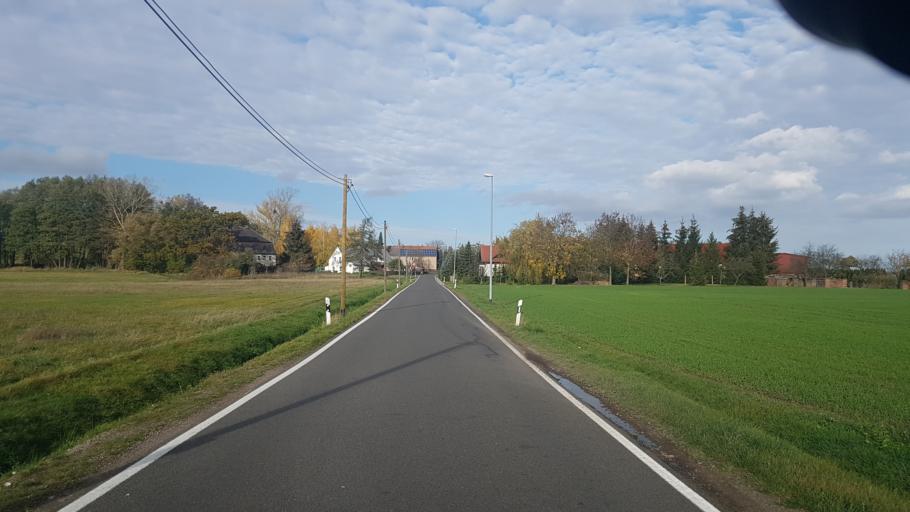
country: DE
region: Saxony
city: Dahlen
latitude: 51.3623
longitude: 13.0380
